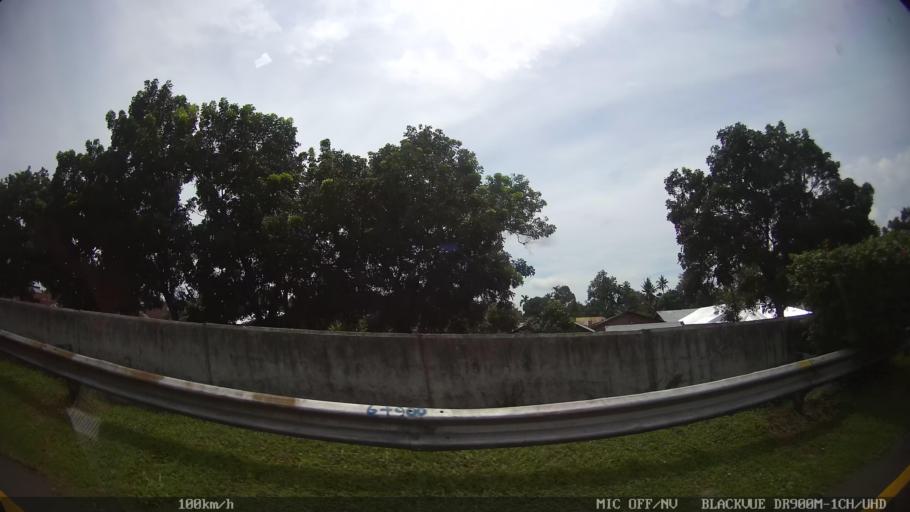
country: ID
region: North Sumatra
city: Labuhan Deli
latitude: 3.7066
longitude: 98.6816
